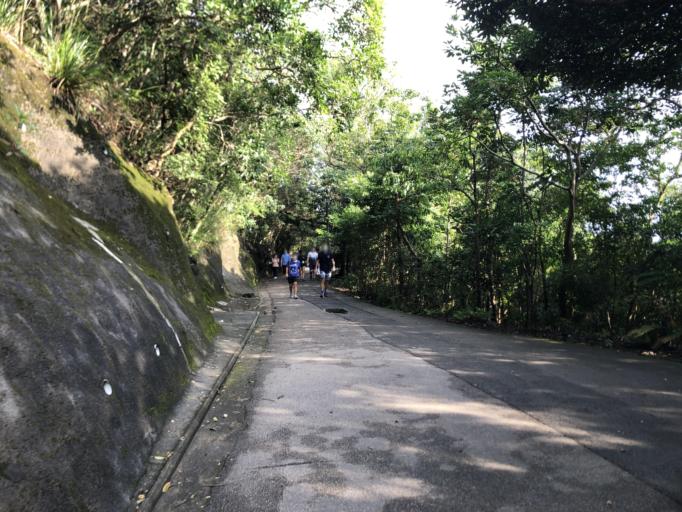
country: HK
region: Central and Western
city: Central
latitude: 22.2727
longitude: 114.1406
